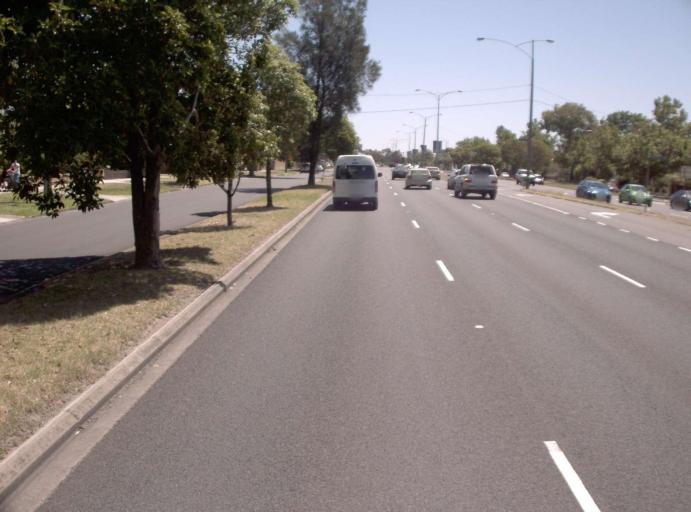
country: AU
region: Victoria
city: Carnegie
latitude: -37.8846
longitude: 145.0619
